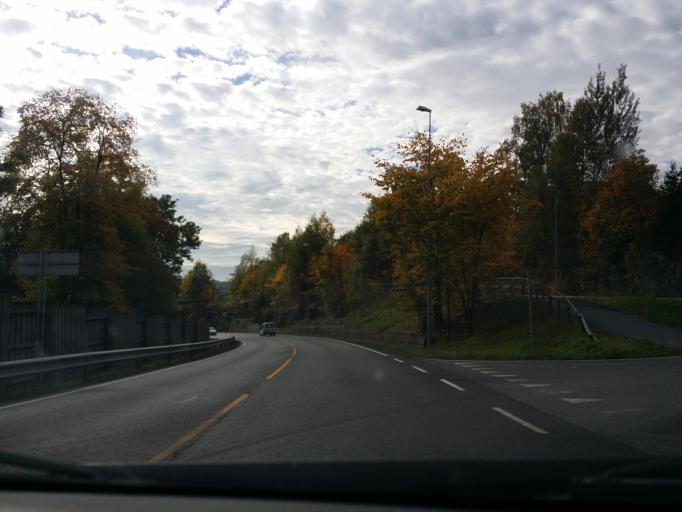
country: NO
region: Akershus
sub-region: Baerum
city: Skui
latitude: 59.9303
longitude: 10.4955
